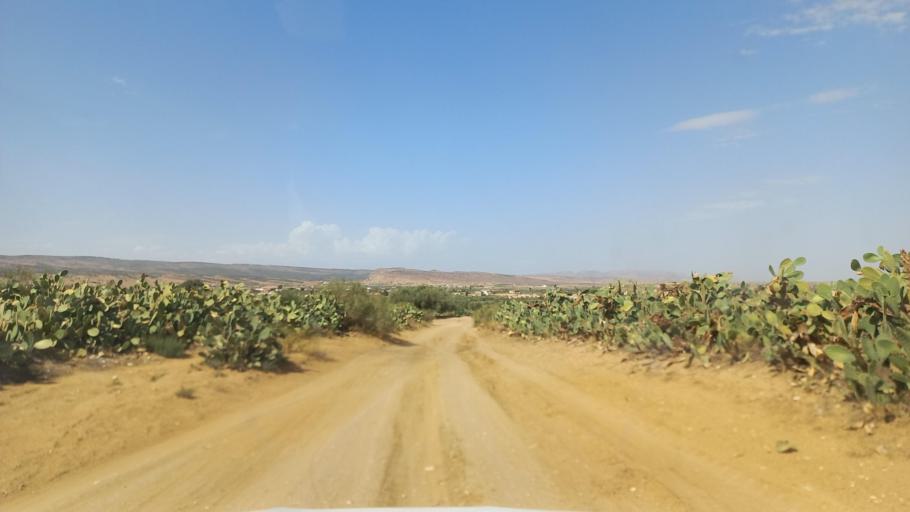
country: TN
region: Al Qasrayn
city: Kasserine
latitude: 35.2739
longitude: 8.9474
